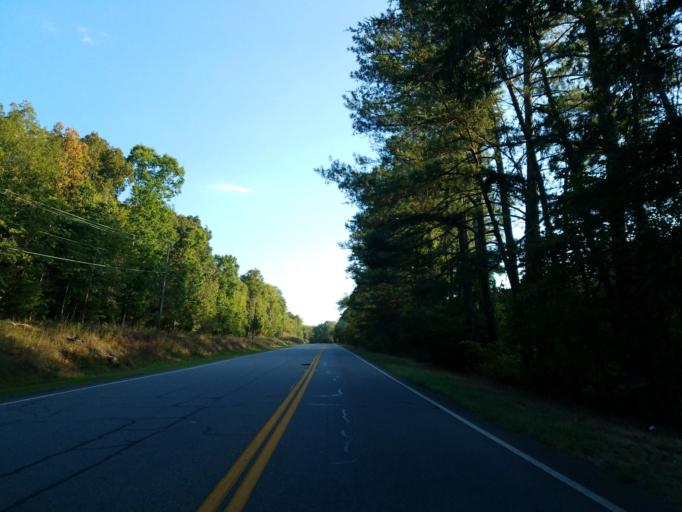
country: US
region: Georgia
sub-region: Bartow County
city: Rydal
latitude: 34.5487
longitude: -84.7074
